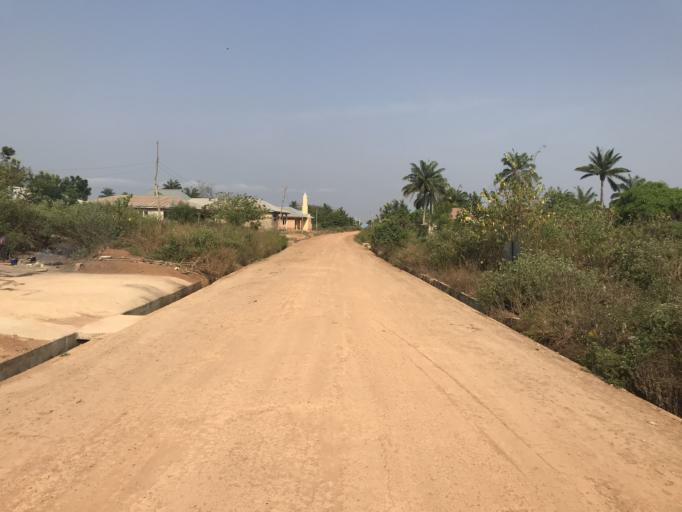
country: NG
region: Osun
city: Iwo
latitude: 7.6165
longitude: 4.1531
